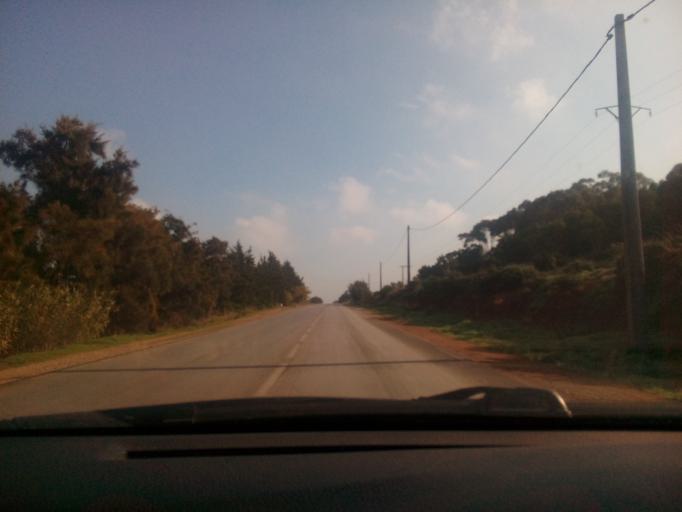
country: DZ
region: Oran
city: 'Ain el Turk
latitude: 35.7043
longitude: -0.8329
